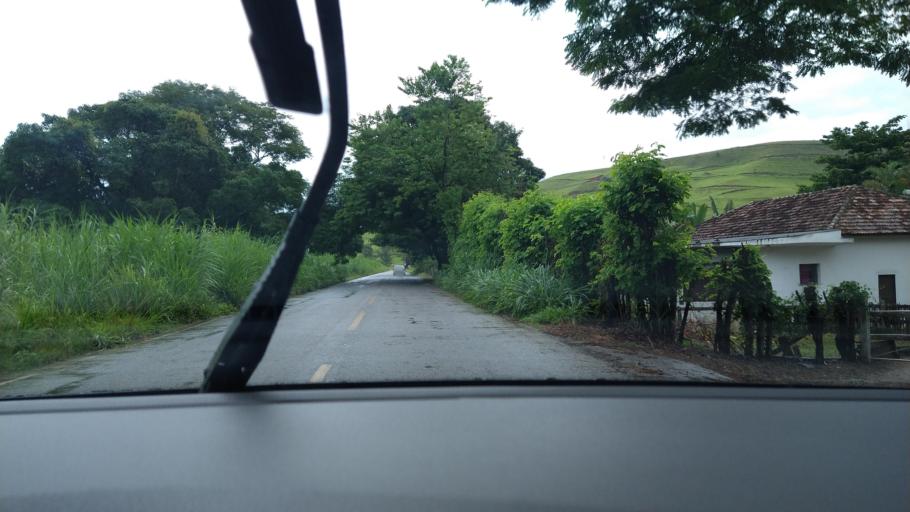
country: BR
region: Minas Gerais
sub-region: Ponte Nova
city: Ponte Nova
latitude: -20.3705
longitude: -42.8951
